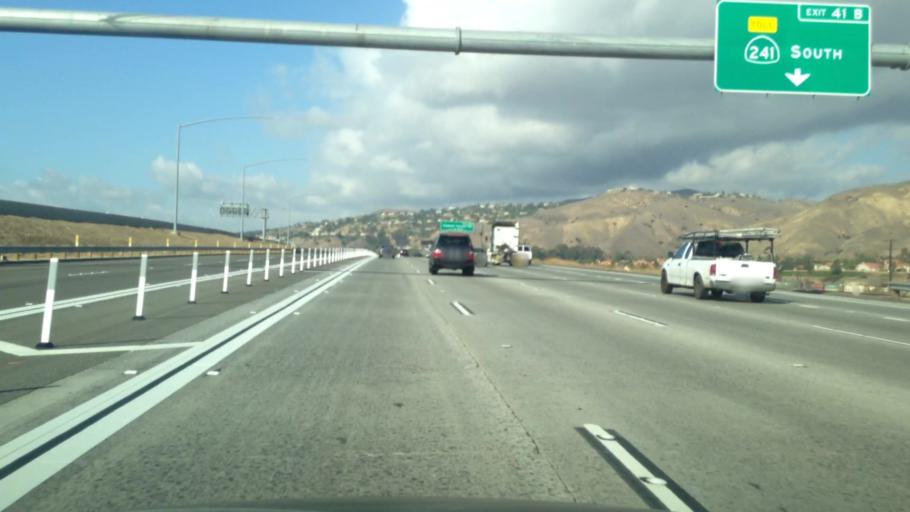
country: US
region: California
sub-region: San Bernardino County
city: Los Serranos
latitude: 33.8714
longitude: -117.6851
